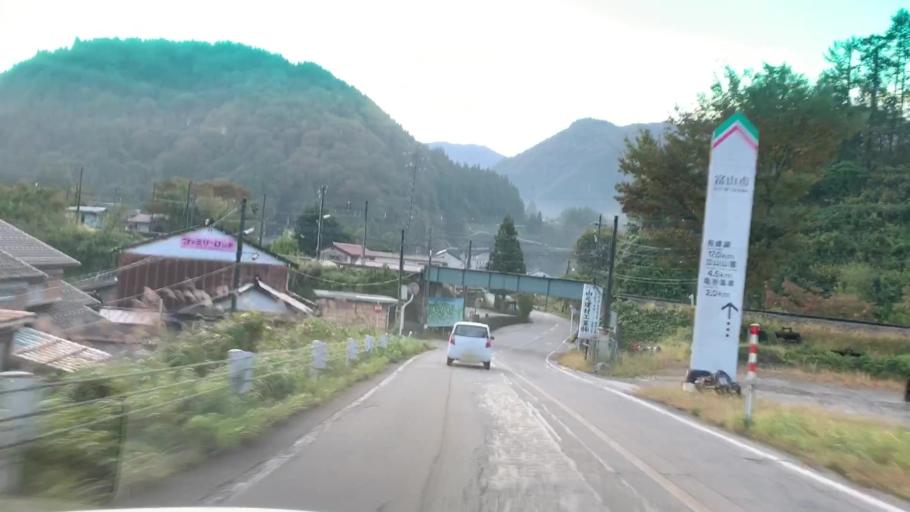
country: JP
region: Toyama
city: Kamiichi
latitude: 36.5733
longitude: 137.3786
